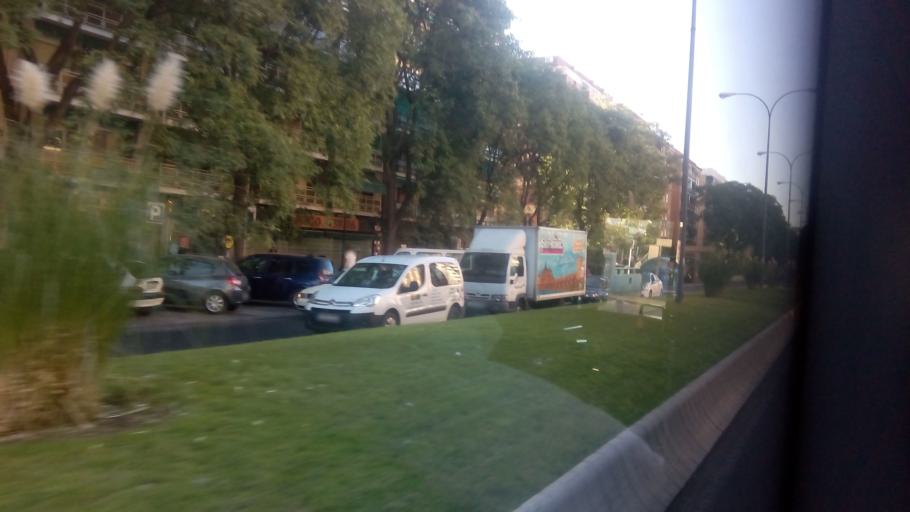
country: ES
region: Andalusia
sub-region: Province of Cordoba
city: Cordoba
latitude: 37.8899
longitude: -4.7645
